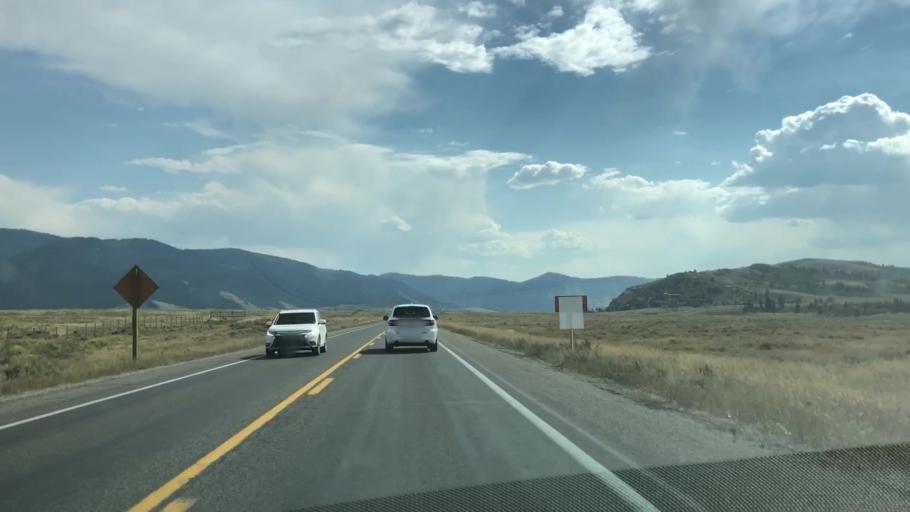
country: US
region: Wyoming
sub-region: Teton County
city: Jackson
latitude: 43.5555
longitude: -110.7330
